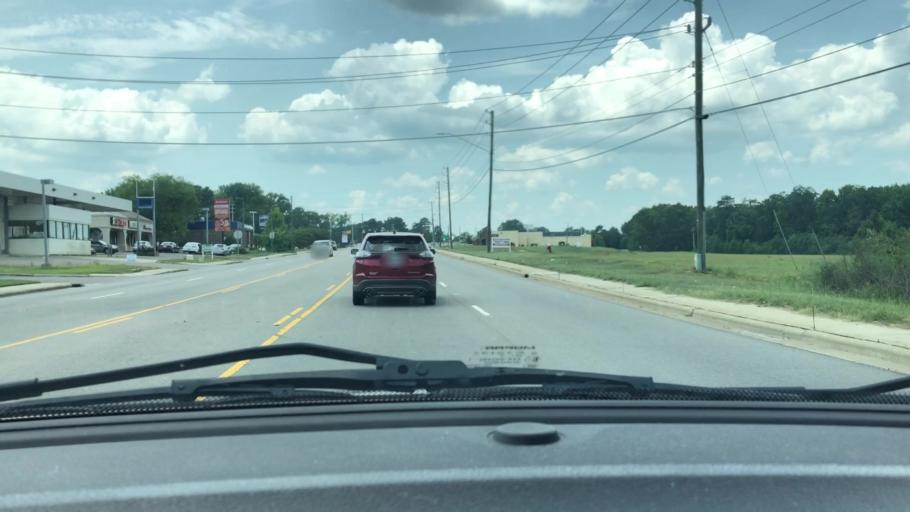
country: US
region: North Carolina
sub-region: Lee County
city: Sanford
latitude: 35.4653
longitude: -79.1551
